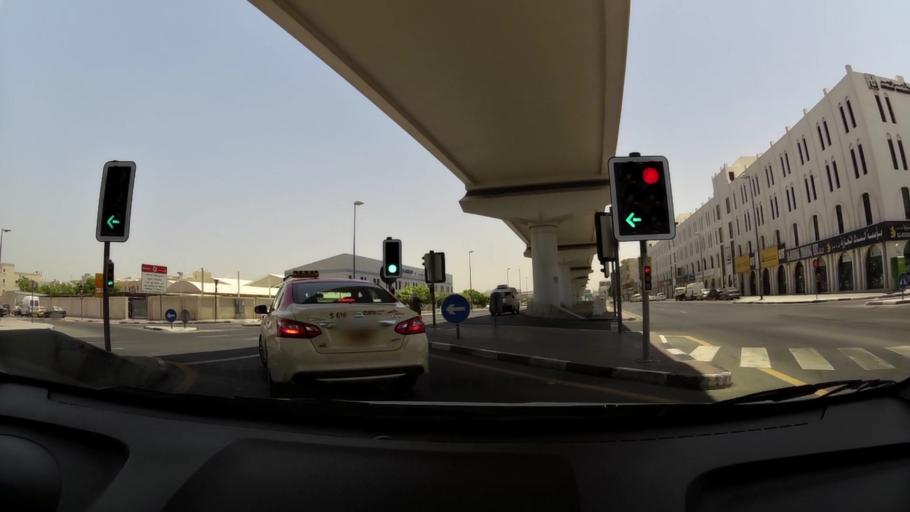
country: AE
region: Ash Shariqah
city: Sharjah
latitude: 25.2720
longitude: 55.3375
